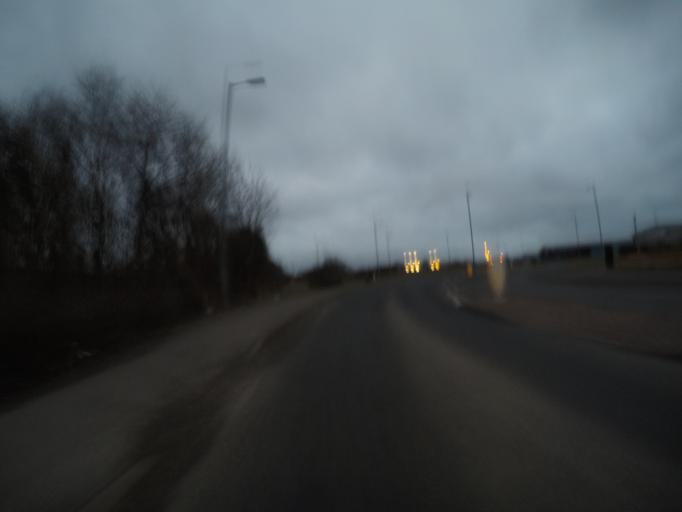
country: GB
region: Scotland
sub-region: North Ayrshire
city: Kilwinning
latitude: 55.6472
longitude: -4.6974
